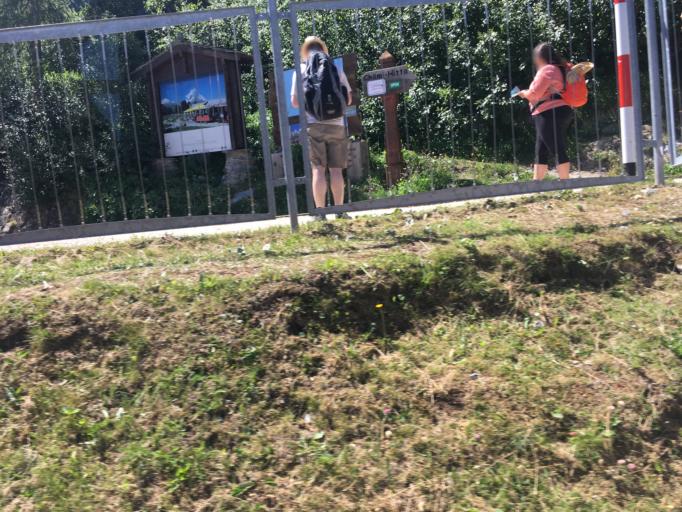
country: CH
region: Valais
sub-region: Visp District
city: Zermatt
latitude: 46.0049
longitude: 7.7534
